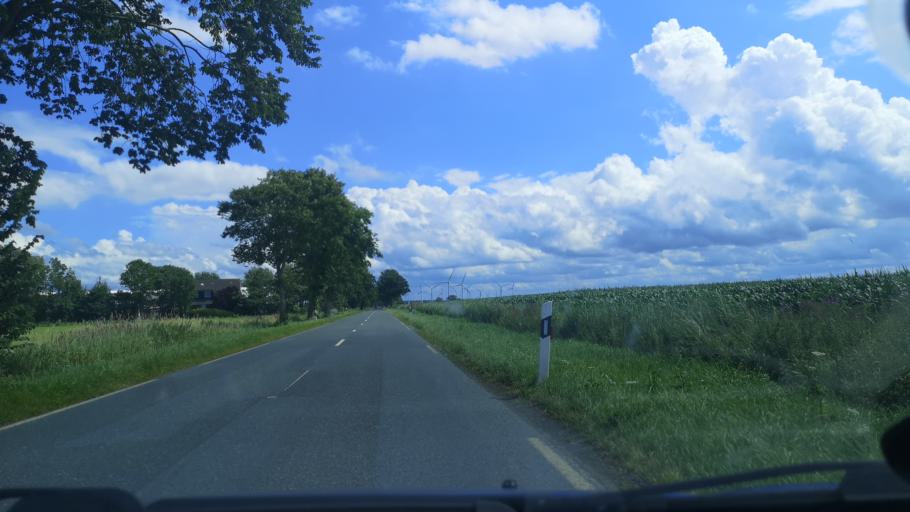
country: DE
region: Lower Saxony
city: Wremen
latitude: 53.6471
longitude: 8.5340
